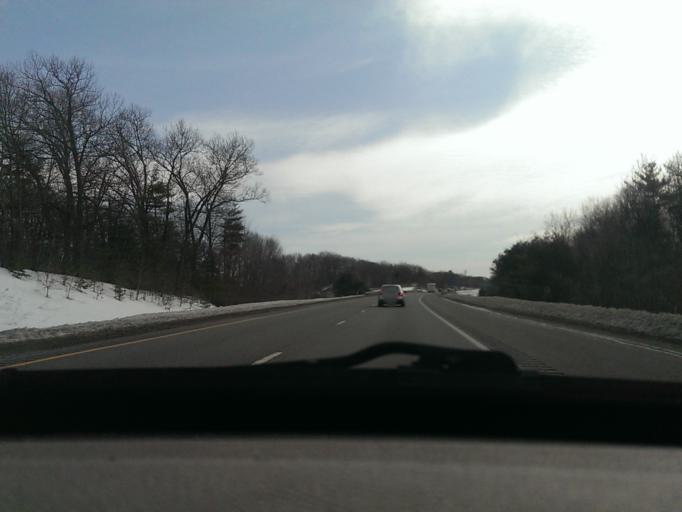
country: US
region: Massachusetts
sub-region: Worcester County
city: Whitinsville
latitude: 42.1173
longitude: -71.7064
